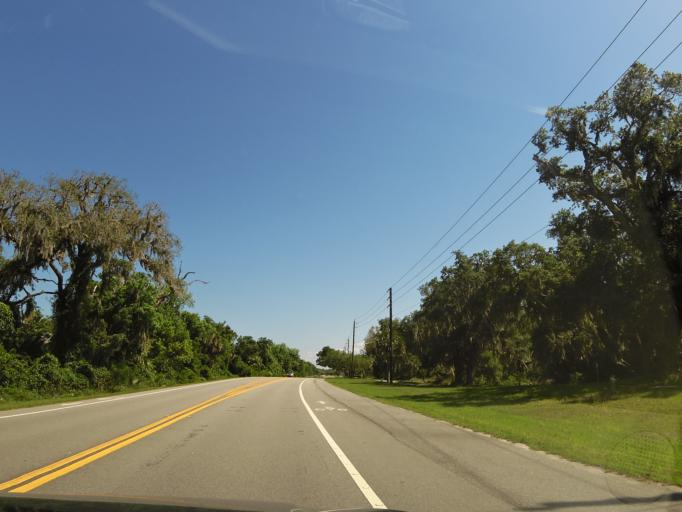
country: US
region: Florida
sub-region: Flagler County
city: Flagler Beach
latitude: 29.4260
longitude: -81.1516
